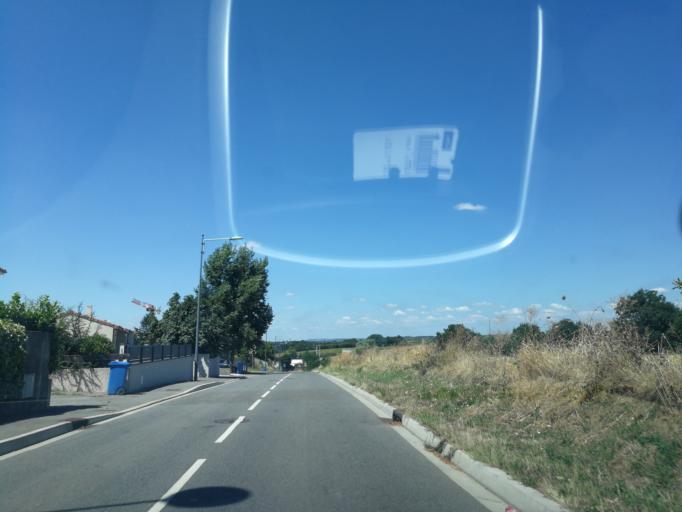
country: FR
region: Midi-Pyrenees
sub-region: Departement de la Haute-Garonne
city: Balma
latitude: 43.6226
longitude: 1.4995
